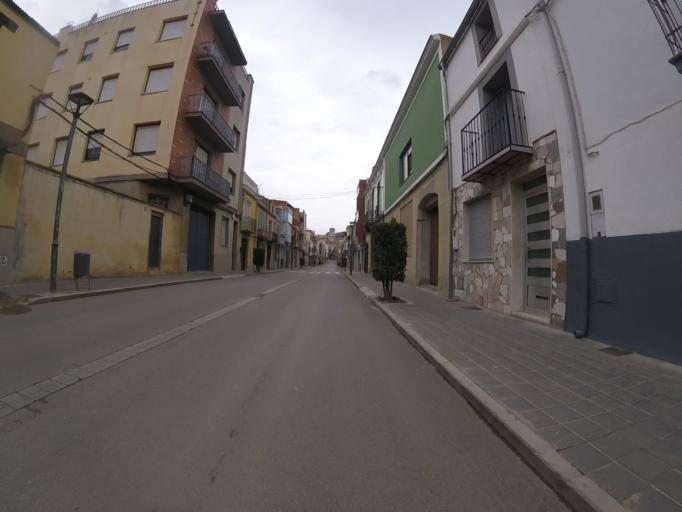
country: ES
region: Valencia
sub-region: Provincia de Castello
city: Cuevas de Vinroma
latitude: 40.3086
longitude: 0.1191
